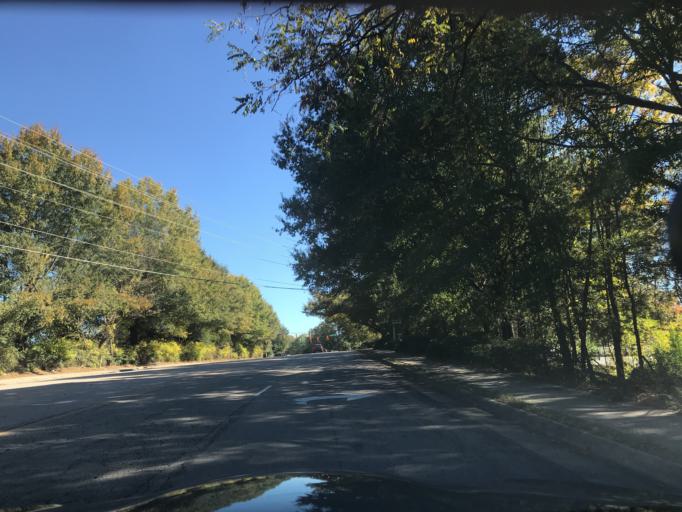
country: US
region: North Carolina
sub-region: Durham County
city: Durham
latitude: 36.0074
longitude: -78.9316
